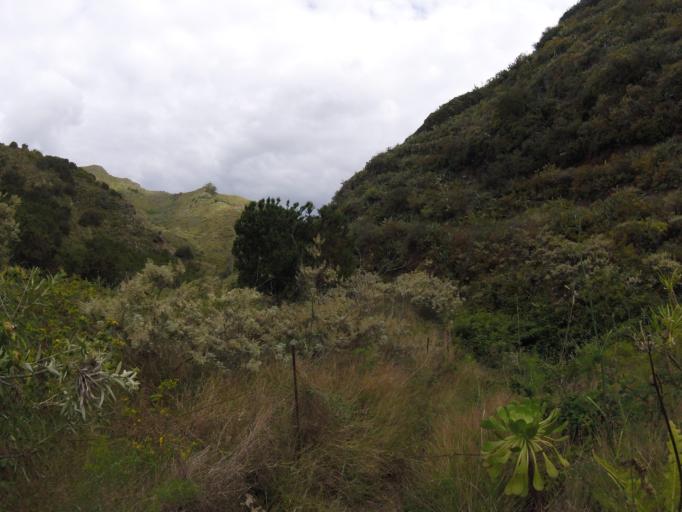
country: ES
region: Canary Islands
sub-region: Provincia de Santa Cruz de Tenerife
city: Tegueste
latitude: 28.5496
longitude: -16.2900
